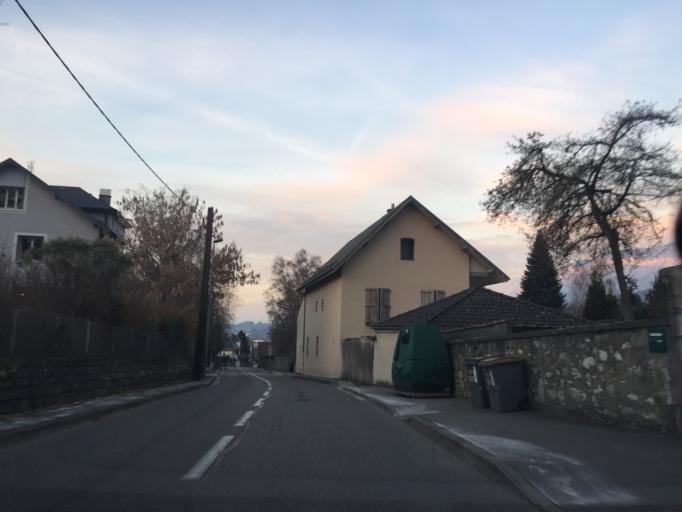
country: FR
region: Rhone-Alpes
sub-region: Departement de la Savoie
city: Jacob-Bellecombette
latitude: 45.5669
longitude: 5.9091
